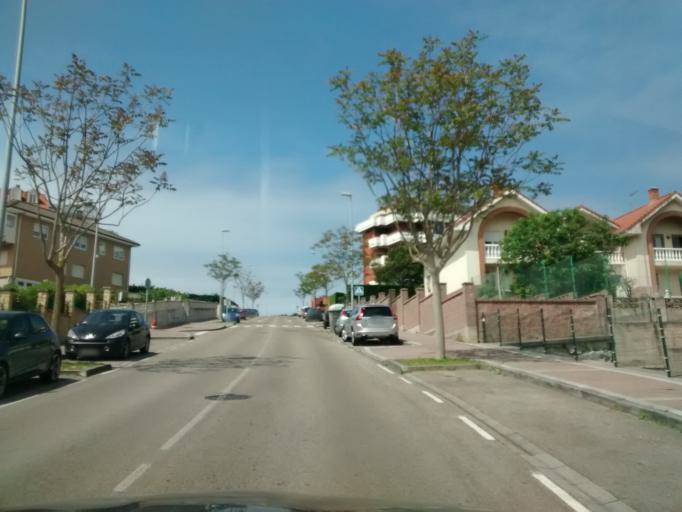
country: ES
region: Cantabria
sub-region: Provincia de Cantabria
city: Santander
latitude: 43.4769
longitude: -3.8040
